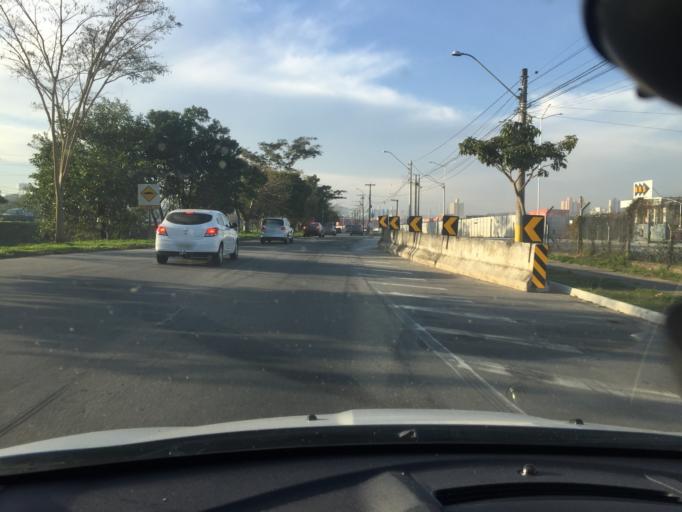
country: BR
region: Sao Paulo
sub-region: Jundiai
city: Jundiai
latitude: -23.1941
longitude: -46.8695
